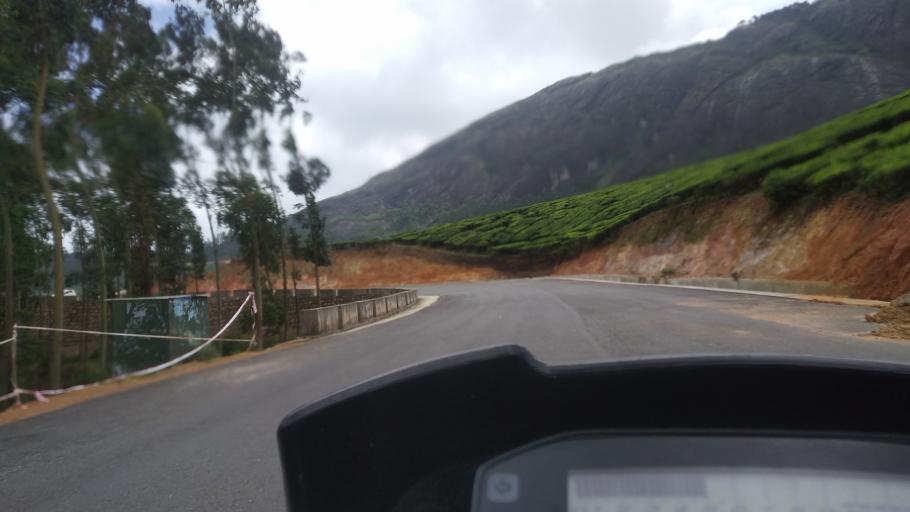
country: IN
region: Kerala
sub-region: Idukki
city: Munnar
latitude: 10.0466
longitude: 77.1139
